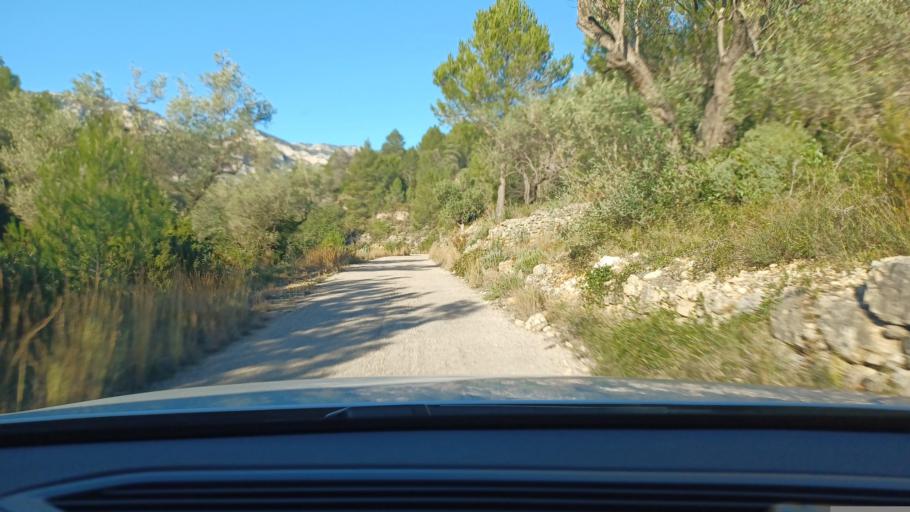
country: ES
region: Catalonia
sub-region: Provincia de Tarragona
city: Mas de Barberans
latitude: 40.7214
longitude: 0.3459
